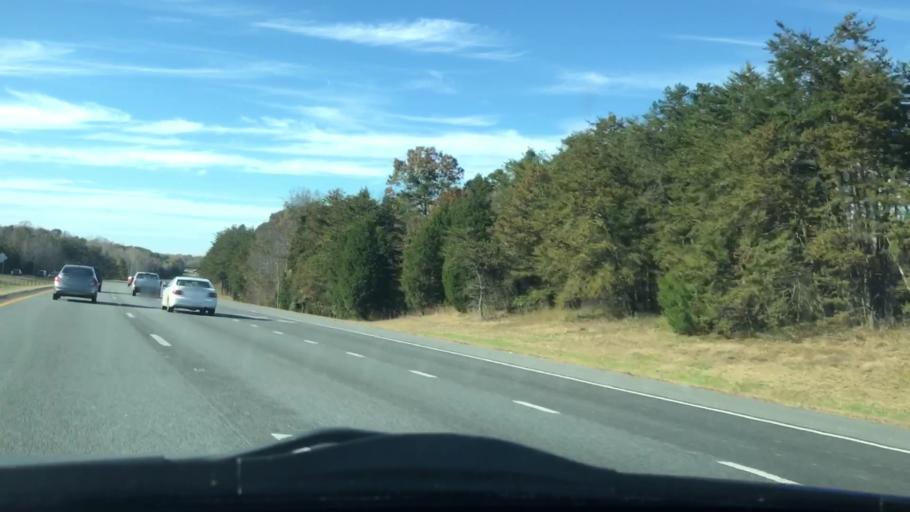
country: US
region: North Carolina
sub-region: Guilford County
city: High Point
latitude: 36.0188
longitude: -80.0463
